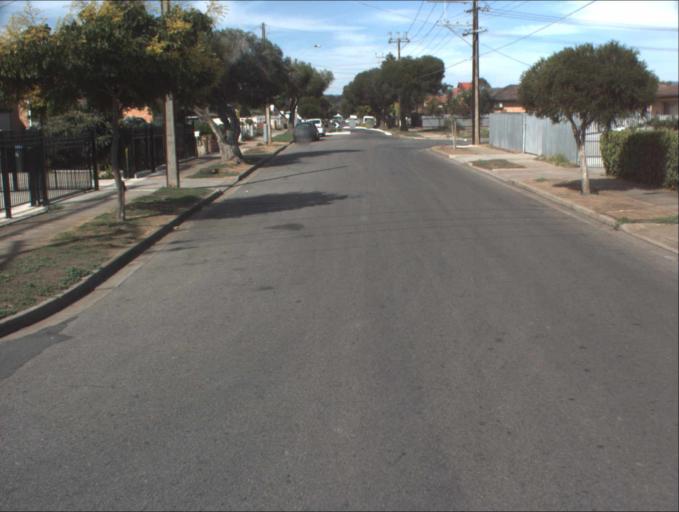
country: AU
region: South Australia
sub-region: Port Adelaide Enfield
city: Blair Athol
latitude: -34.8599
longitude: 138.5843
